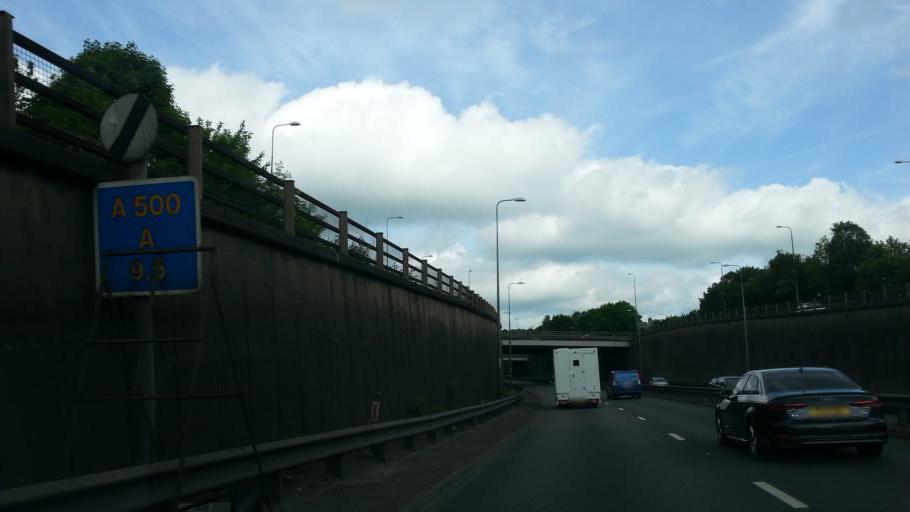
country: GB
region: England
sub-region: Staffordshire
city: Newcastle under Lyme
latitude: 53.0390
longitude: -2.2134
